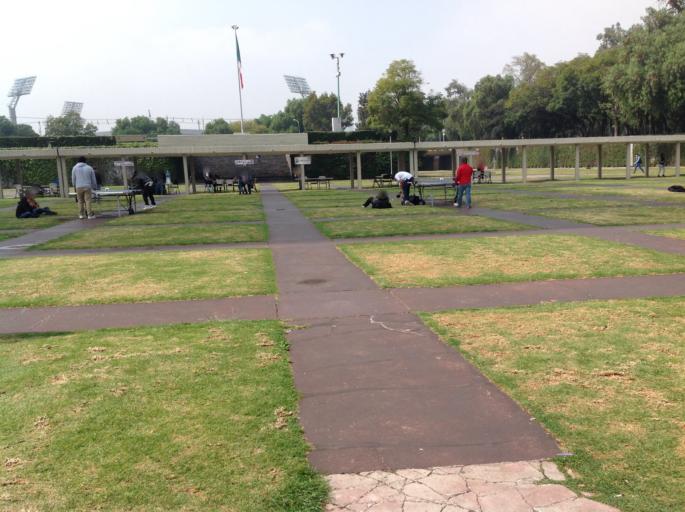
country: MX
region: Mexico City
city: Magdalena Contreras
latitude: 19.3328
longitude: -99.1879
